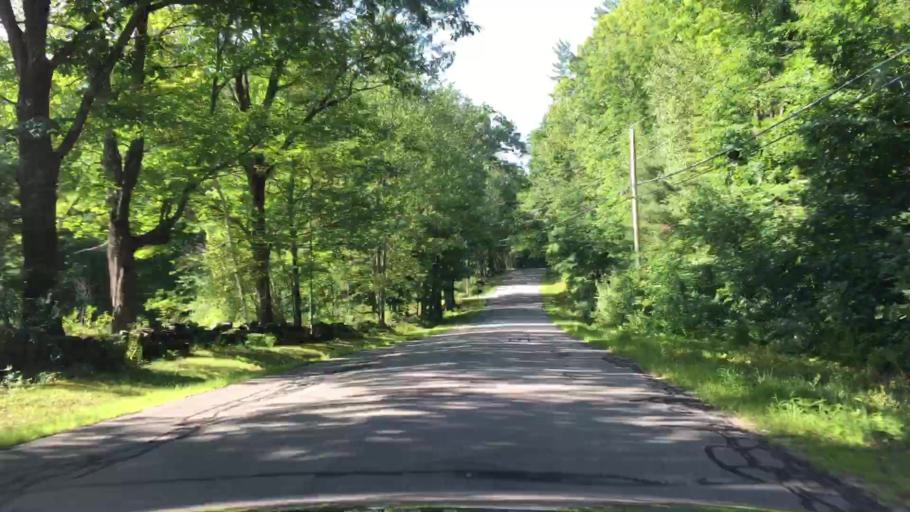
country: US
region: New Hampshire
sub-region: Grafton County
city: Ashland
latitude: 43.7128
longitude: -71.6300
